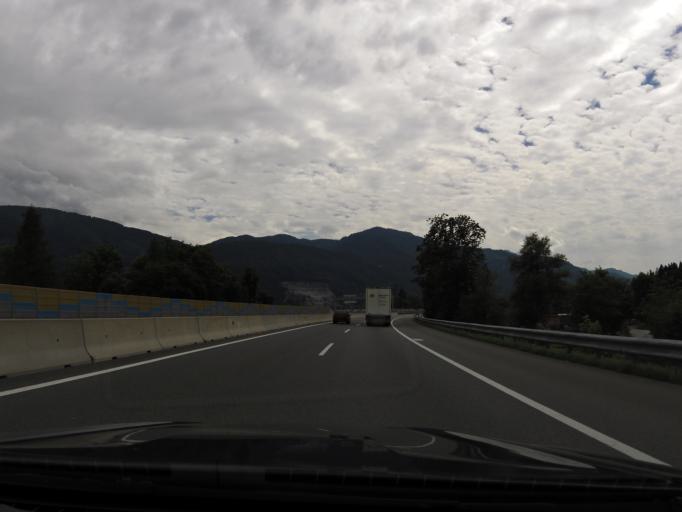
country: AT
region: Tyrol
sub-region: Politischer Bezirk Kufstein
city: Angath
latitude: 47.4941
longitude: 12.0579
